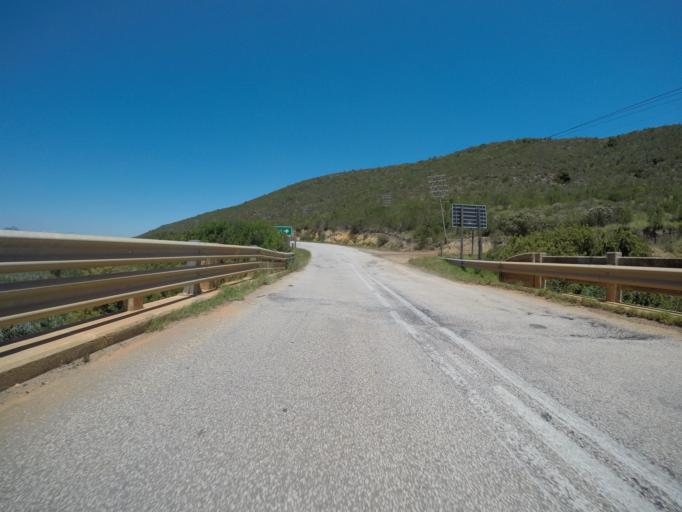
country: ZA
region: Eastern Cape
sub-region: Cacadu District Municipality
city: Kareedouw
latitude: -33.8785
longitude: 24.0533
